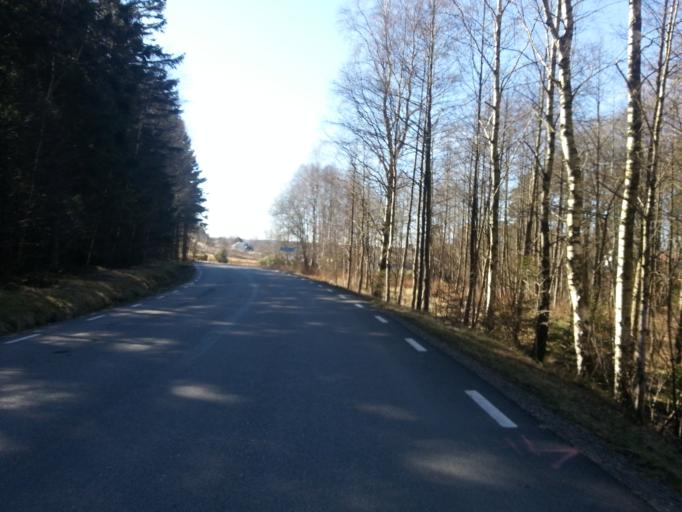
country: SE
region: Vaestra Goetaland
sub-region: Kungalvs Kommun
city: Kungalv
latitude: 57.9065
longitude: 11.9445
